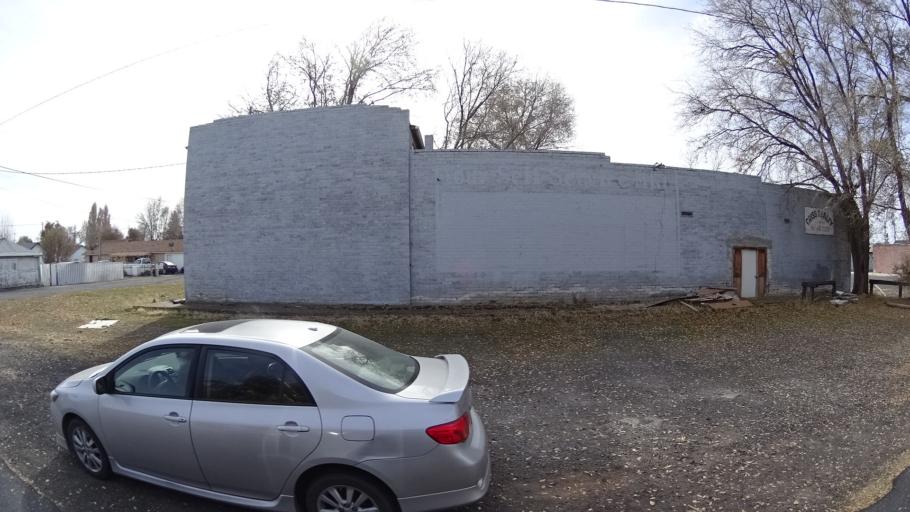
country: US
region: California
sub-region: Siskiyou County
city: Tulelake
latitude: 41.9548
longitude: -121.4764
